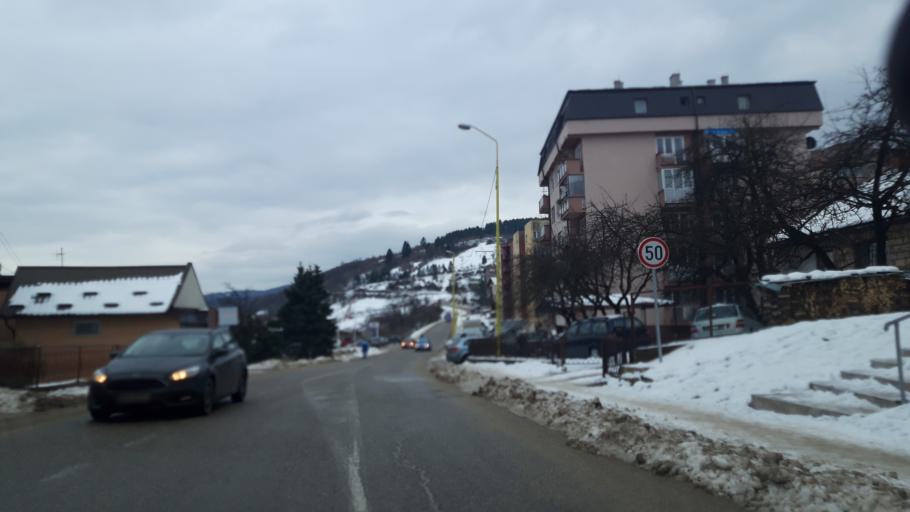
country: BA
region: Republika Srpska
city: Vlasenica
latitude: 44.1831
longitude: 18.9437
